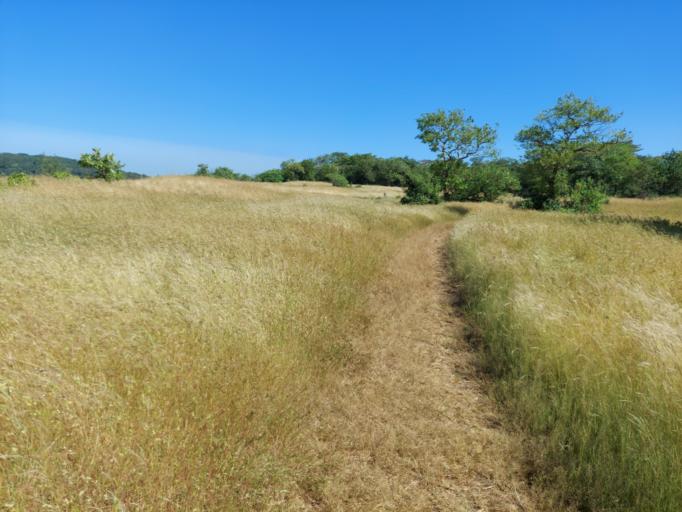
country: IN
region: Maharashtra
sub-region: Sindhudurg
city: Kudal
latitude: 16.0814
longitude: 73.8433
